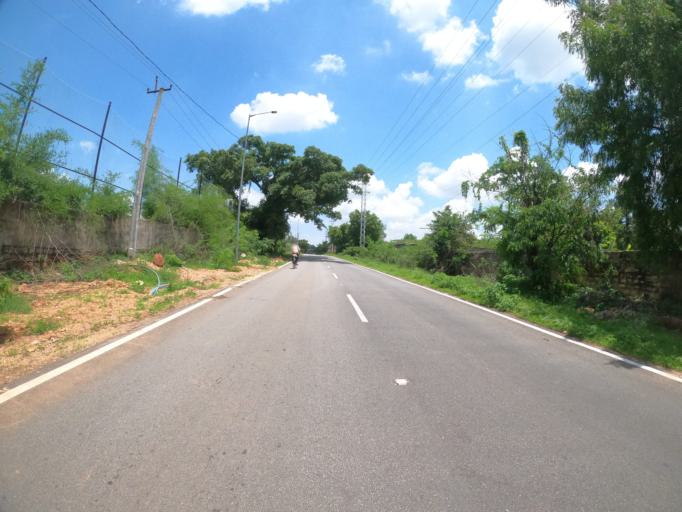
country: IN
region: Telangana
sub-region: Rangareddi
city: Sriramnagar
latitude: 17.3626
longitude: 78.3234
